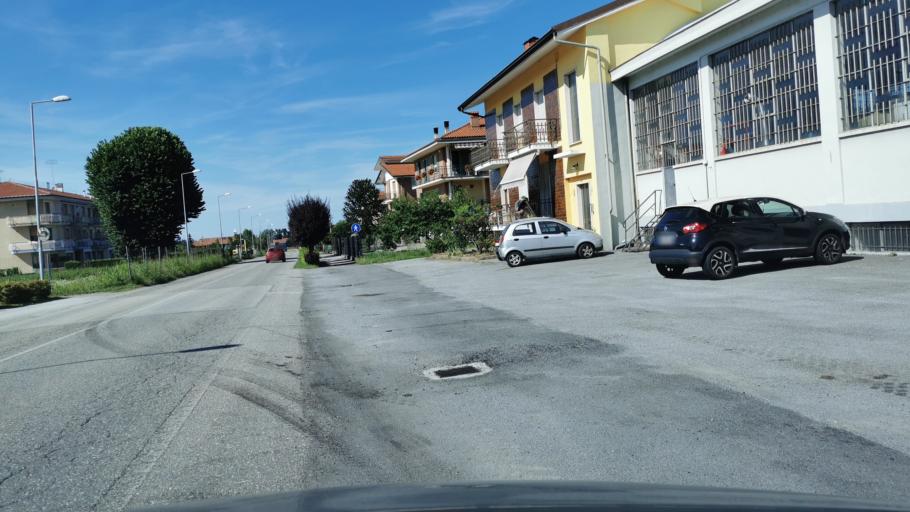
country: IT
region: Piedmont
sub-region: Provincia di Cuneo
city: Boves
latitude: 44.3361
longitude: 7.5565
